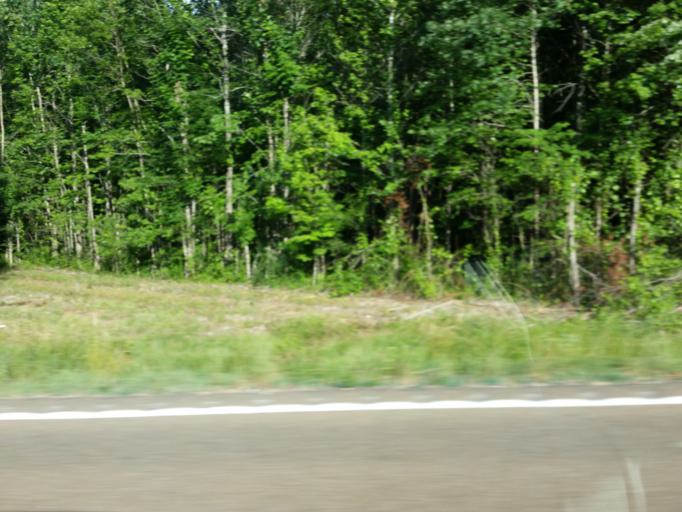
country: US
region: Mississippi
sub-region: Calhoun County
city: Calhoun City
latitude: 33.7919
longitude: -89.3617
